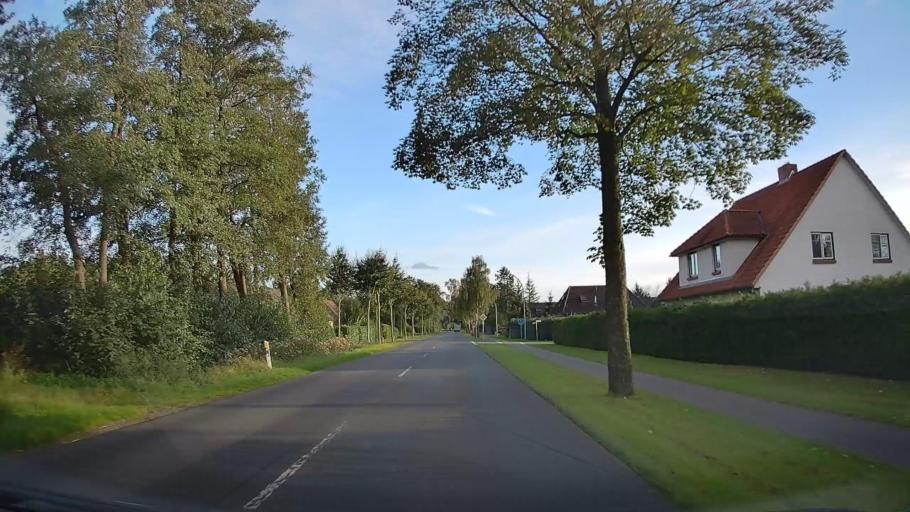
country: DE
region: Lower Saxony
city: Sottrum
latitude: 53.0926
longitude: 9.2360
